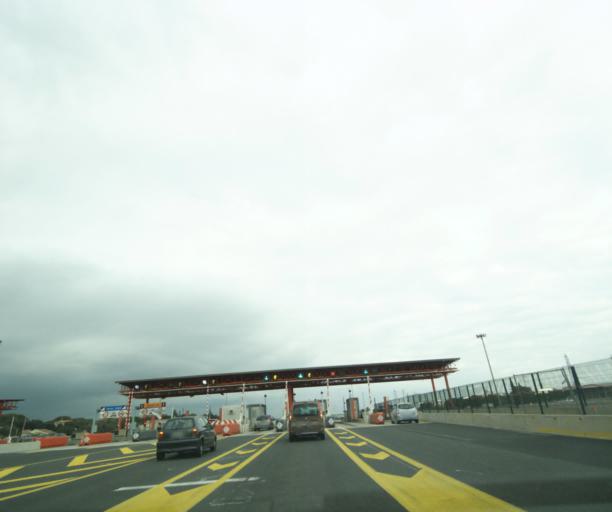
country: FR
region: Languedoc-Roussillon
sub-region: Departement de l'Herault
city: Saint-Jean-de-Vedas
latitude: 43.5619
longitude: 3.8303
